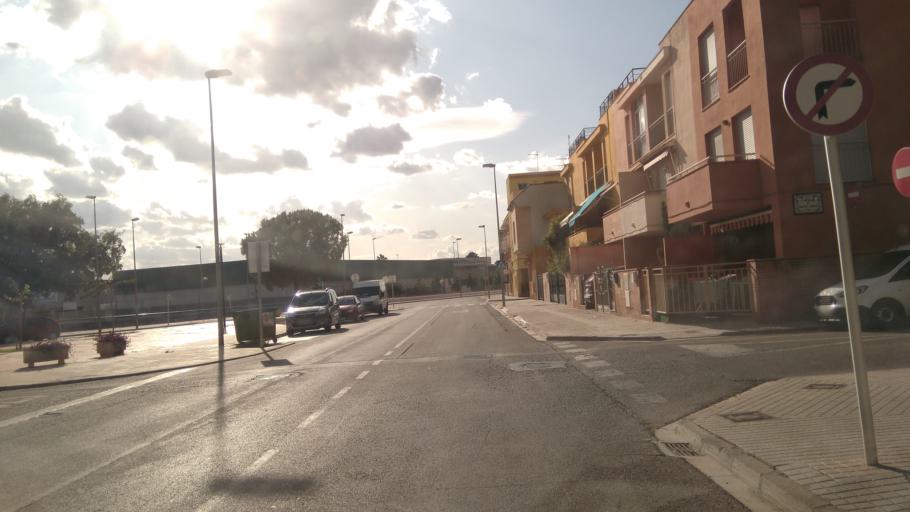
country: ES
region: Valencia
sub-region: Provincia de Valencia
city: L'Alcudia
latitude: 39.1913
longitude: -0.5044
